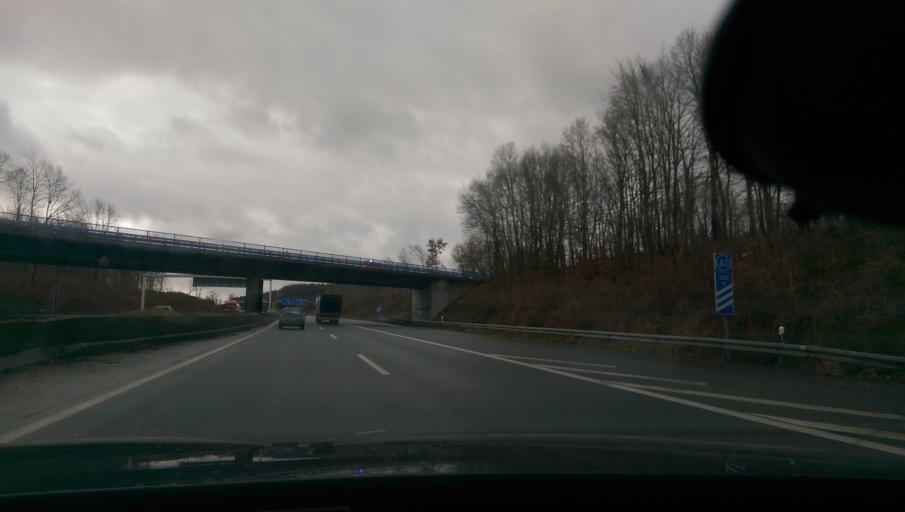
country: DE
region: North Rhine-Westphalia
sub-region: Regierungsbezirk Arnsberg
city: Werl
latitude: 51.5265
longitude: 7.8952
